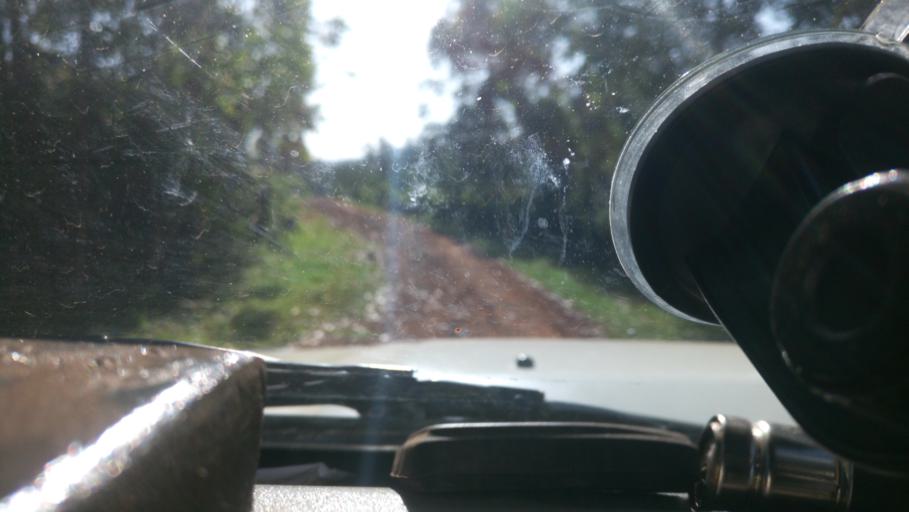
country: KE
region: Kisii
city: Kisii
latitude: -0.6152
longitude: 34.7832
